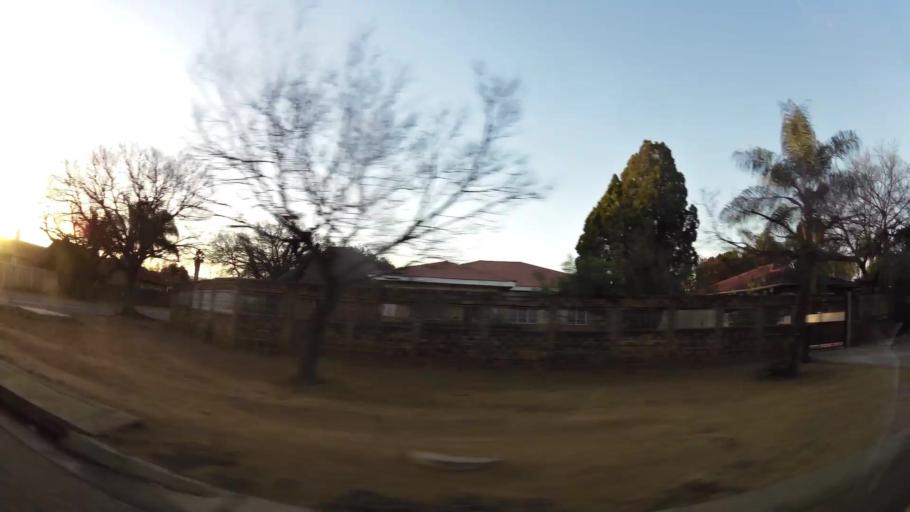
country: ZA
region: Gauteng
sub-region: City of Tshwane Metropolitan Municipality
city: Pretoria
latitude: -25.7115
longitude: 28.2456
